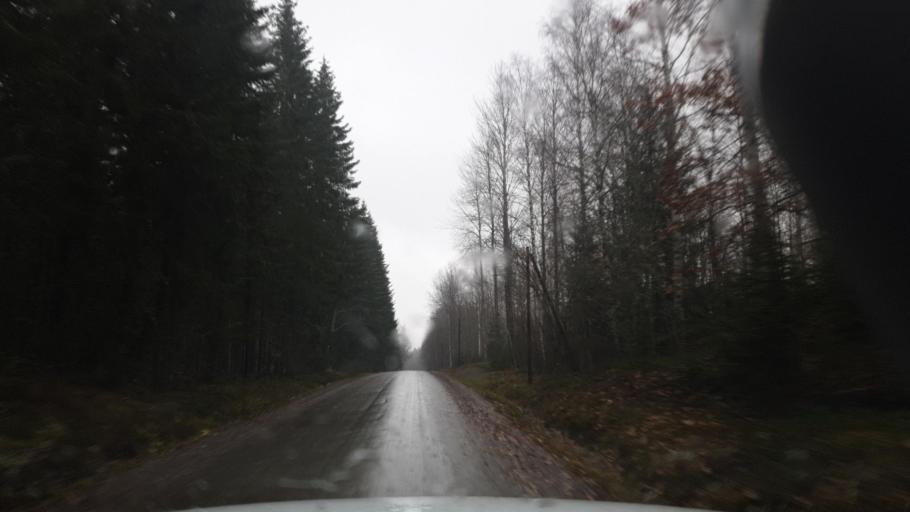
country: SE
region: Vaermland
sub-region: Karlstads Kommun
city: Edsvalla
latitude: 59.5035
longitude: 13.1967
